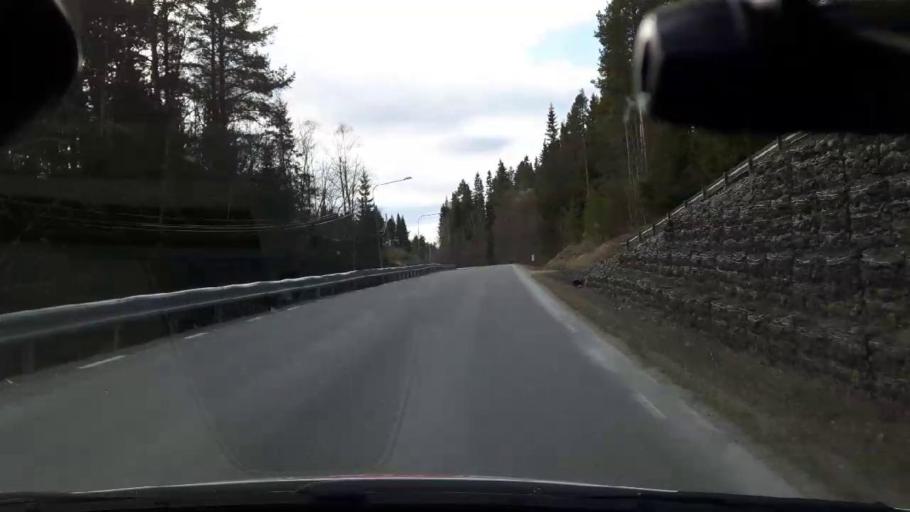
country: SE
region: Jaemtland
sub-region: OEstersunds Kommun
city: Ostersund
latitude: 62.9914
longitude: 14.5921
